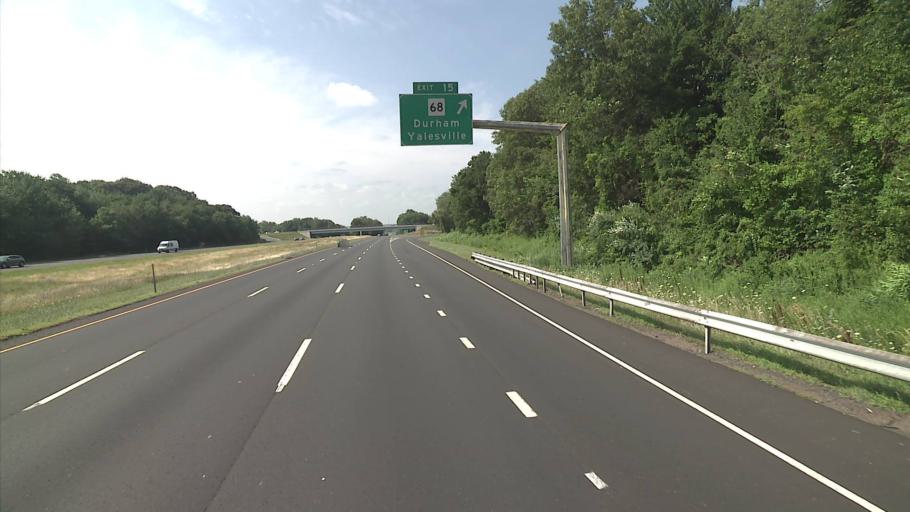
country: US
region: Connecticut
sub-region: New Haven County
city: Wallingford Center
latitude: 41.4845
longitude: -72.7686
